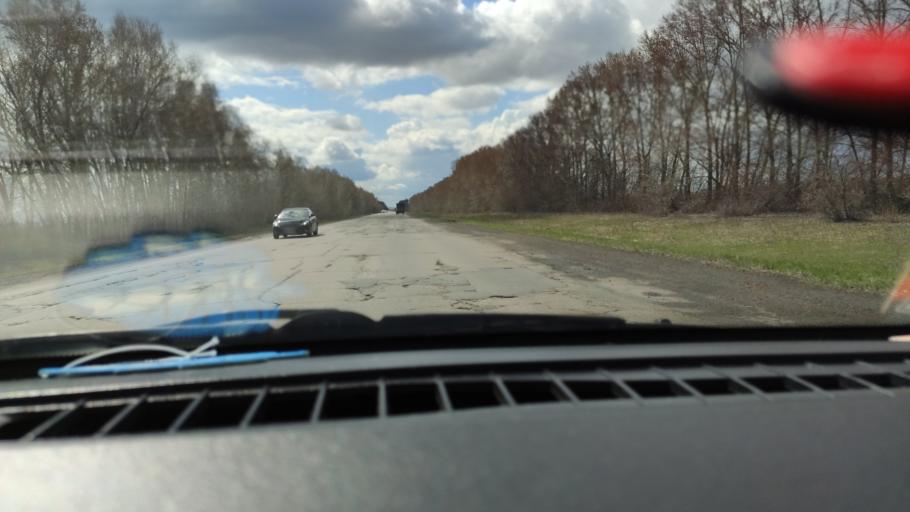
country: RU
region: Samara
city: Tol'yatti
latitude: 53.6389
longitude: 49.4196
